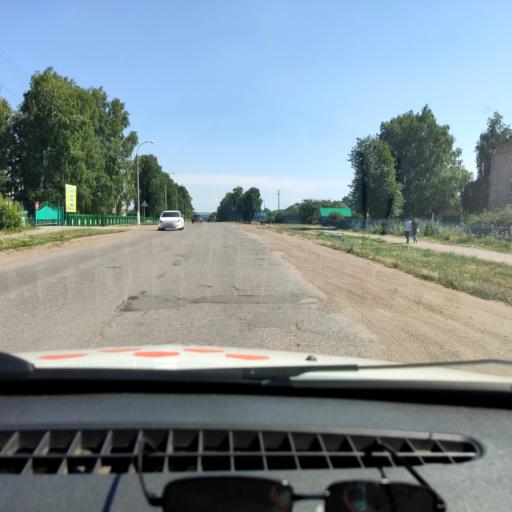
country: RU
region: Bashkortostan
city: Tolbazy
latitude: 54.0102
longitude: 55.8875
